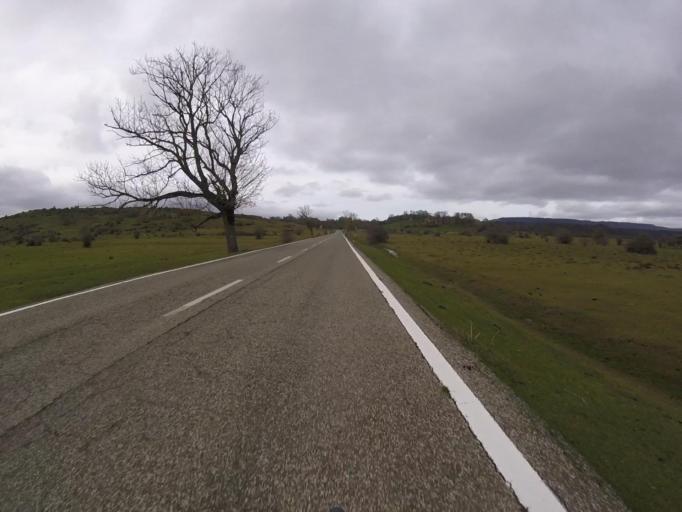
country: ES
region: Navarre
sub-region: Provincia de Navarra
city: Eulate
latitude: 42.8134
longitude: -2.1627
